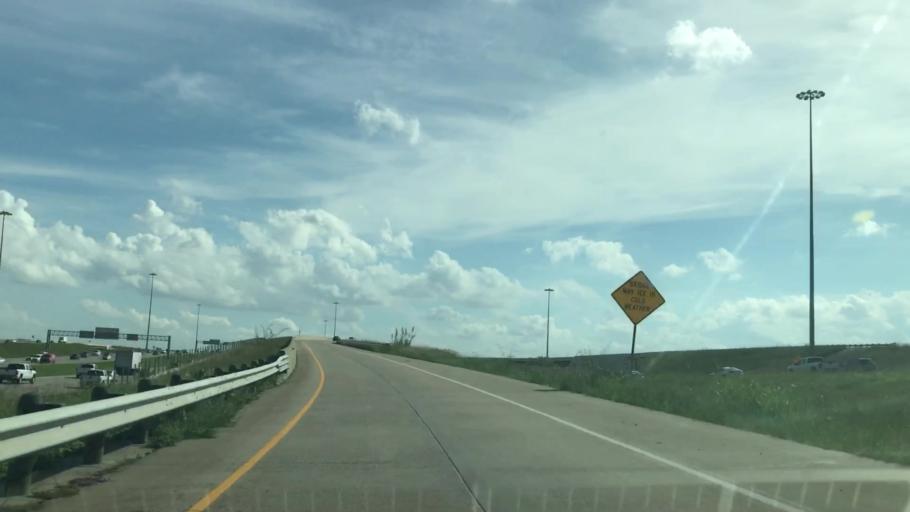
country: US
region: Texas
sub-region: Dallas County
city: Coppell
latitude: 32.9482
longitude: -97.0406
